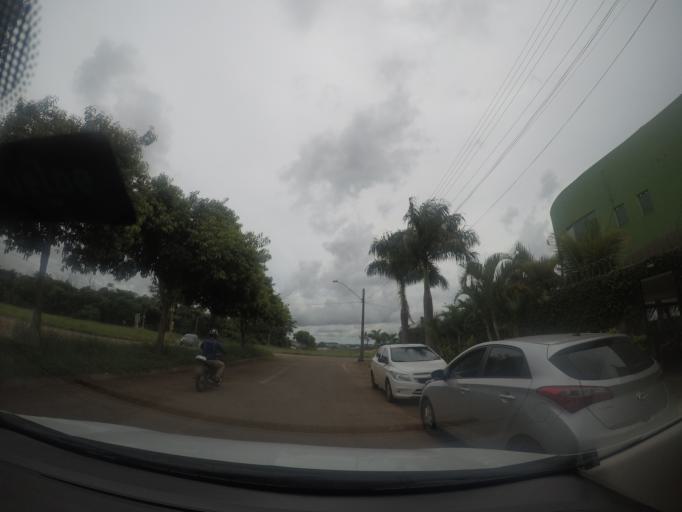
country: BR
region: Goias
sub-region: Trindade
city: Trindade
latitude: -16.6888
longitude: -49.3871
